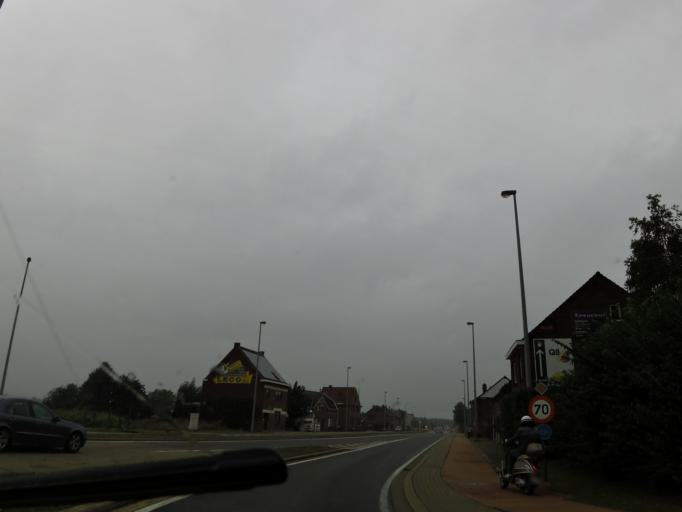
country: NL
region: Limburg
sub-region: Gemeente Stein
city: Berg
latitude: 51.0257
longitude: 5.7272
